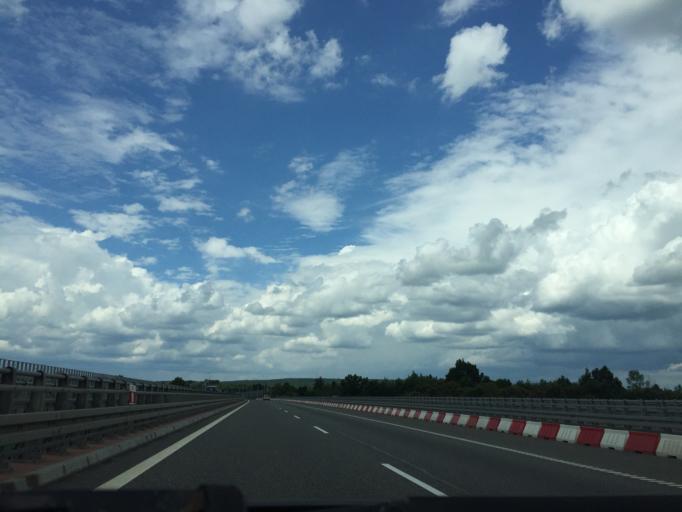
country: PL
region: Swietokrzyskie
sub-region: Powiat skarzyski
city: Skarzysko-Kamienna
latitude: 51.0932
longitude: 20.8360
